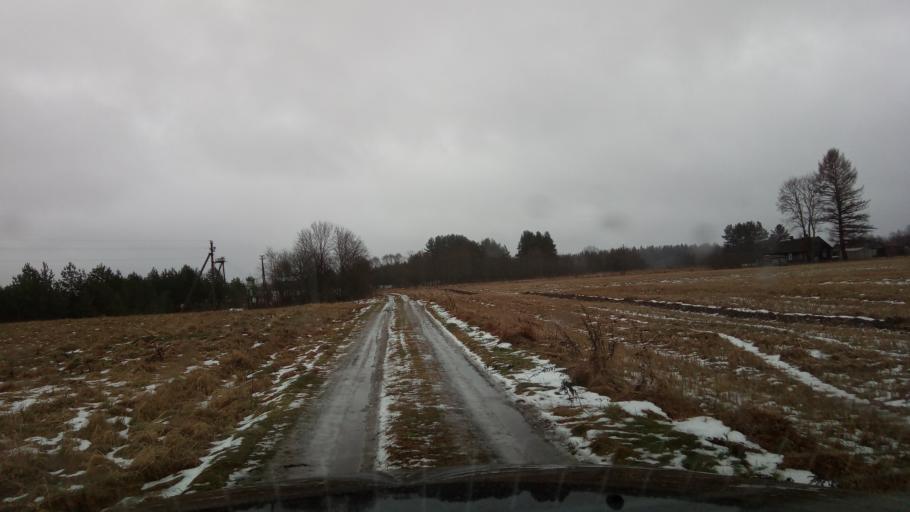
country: LT
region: Utenos apskritis
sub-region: Utena
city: Utena
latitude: 55.3696
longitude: 25.7624
